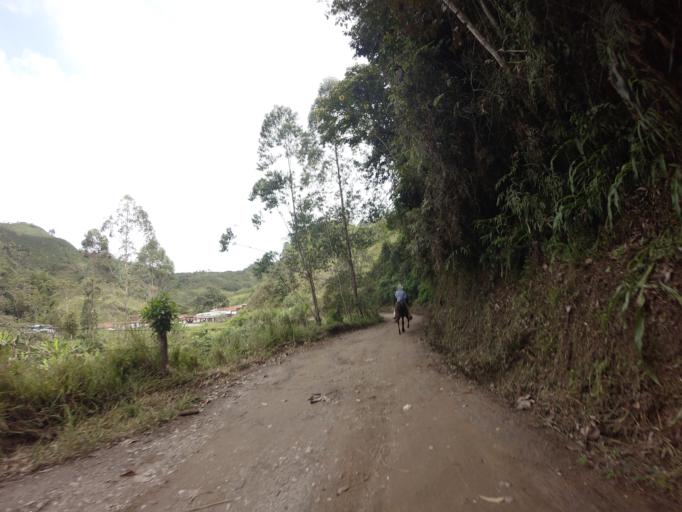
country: CO
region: Caldas
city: Marquetalia
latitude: 5.3022
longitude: -75.0403
